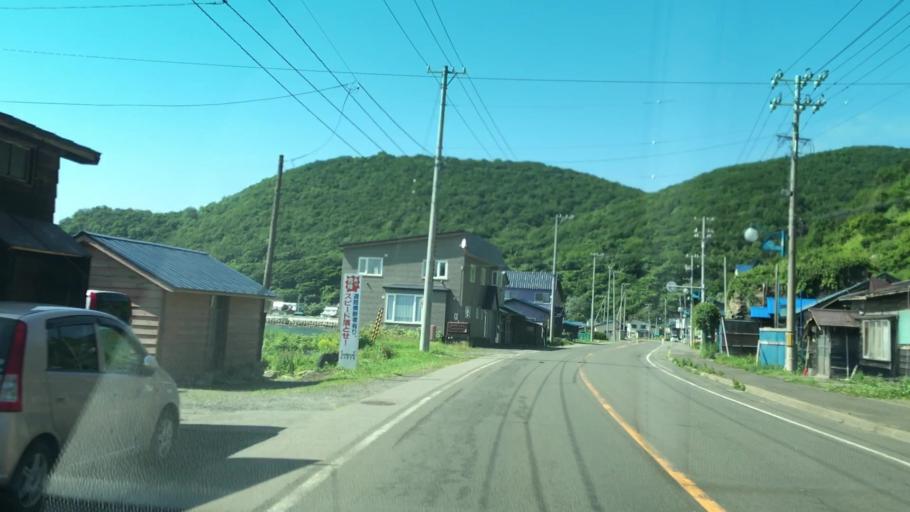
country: JP
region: Hokkaido
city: Iwanai
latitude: 43.1029
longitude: 140.4602
